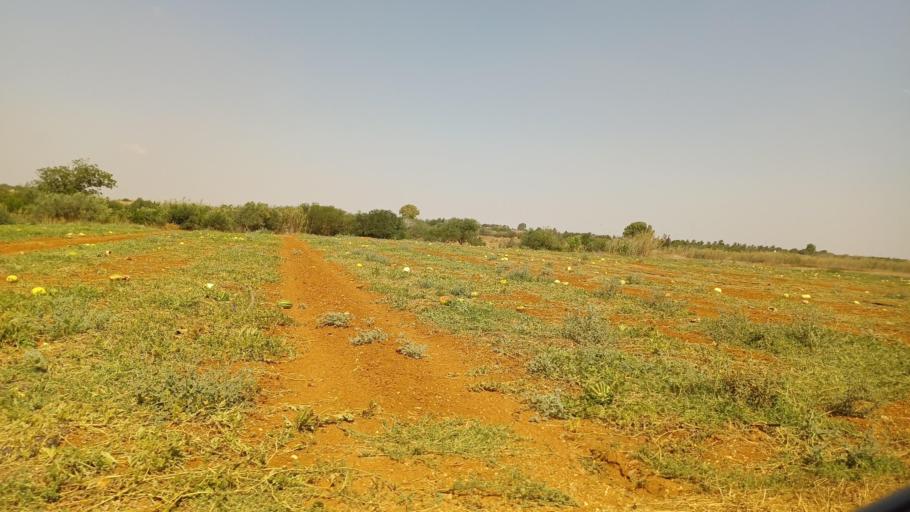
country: CY
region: Ammochostos
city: Frenaros
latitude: 35.0619
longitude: 33.9200
